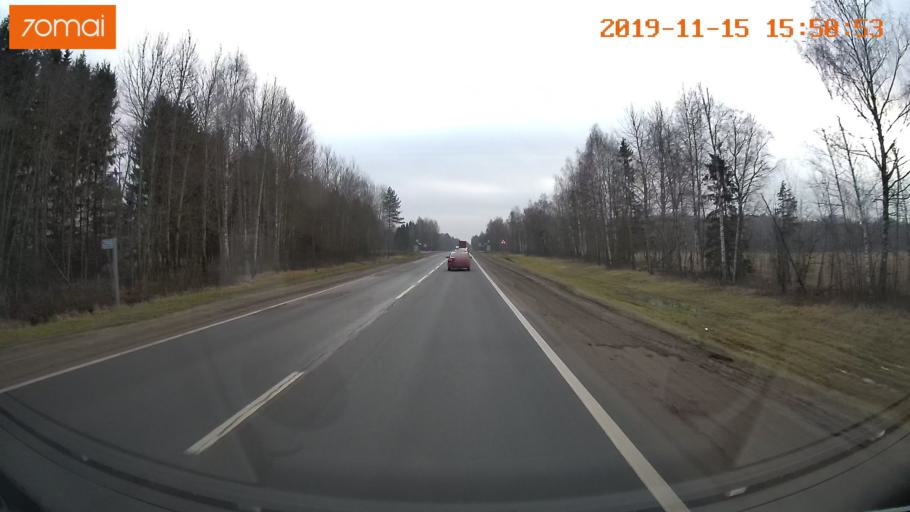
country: RU
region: Jaroslavl
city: Yaroslavl
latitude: 57.9009
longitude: 40.0115
